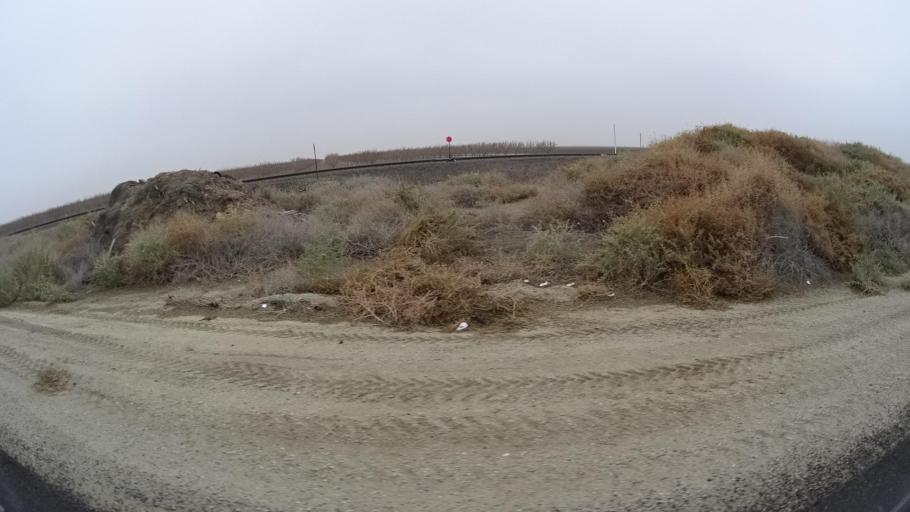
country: US
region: California
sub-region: Kern County
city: Greenfield
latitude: 35.1803
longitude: -119.1898
